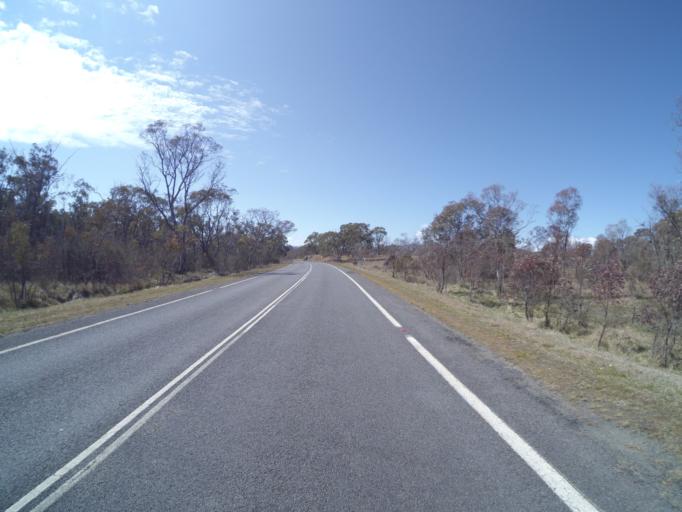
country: AU
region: Australian Capital Territory
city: Macarthur
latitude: -35.4619
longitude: 149.0303
